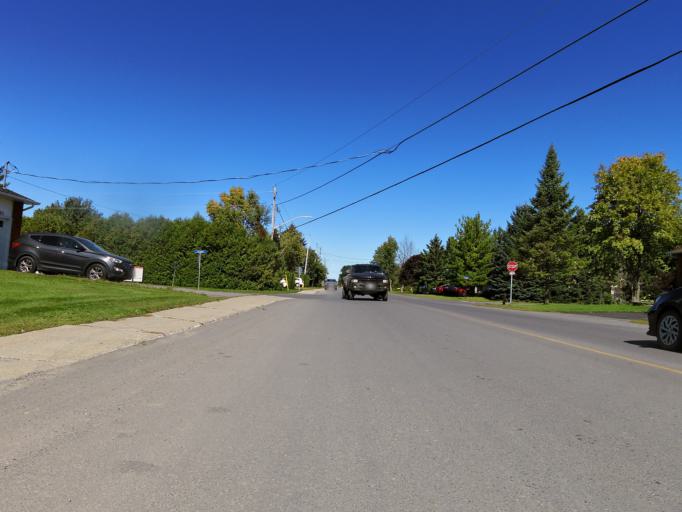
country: CA
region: Ontario
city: Casselman
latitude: 45.2716
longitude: -75.2928
